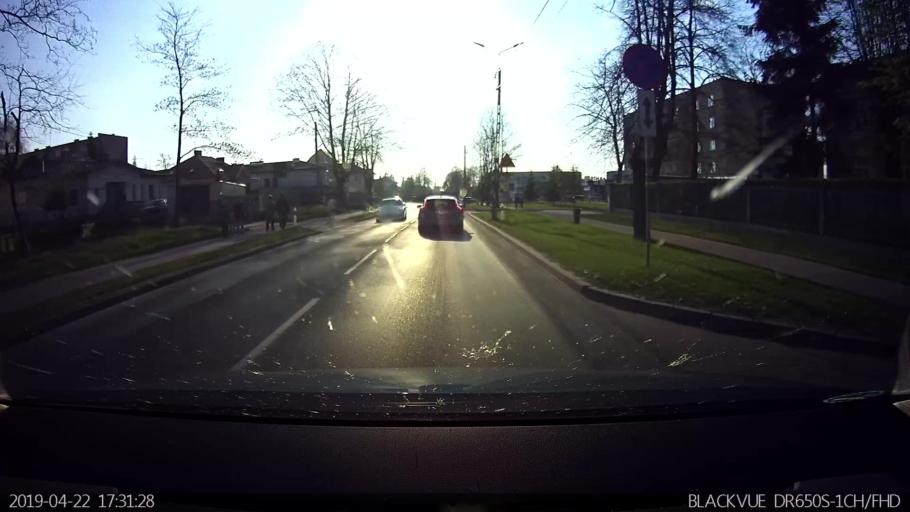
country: PL
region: Masovian Voivodeship
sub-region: Powiat sokolowski
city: Sokolow Podlaski
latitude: 52.4071
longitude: 22.2381
